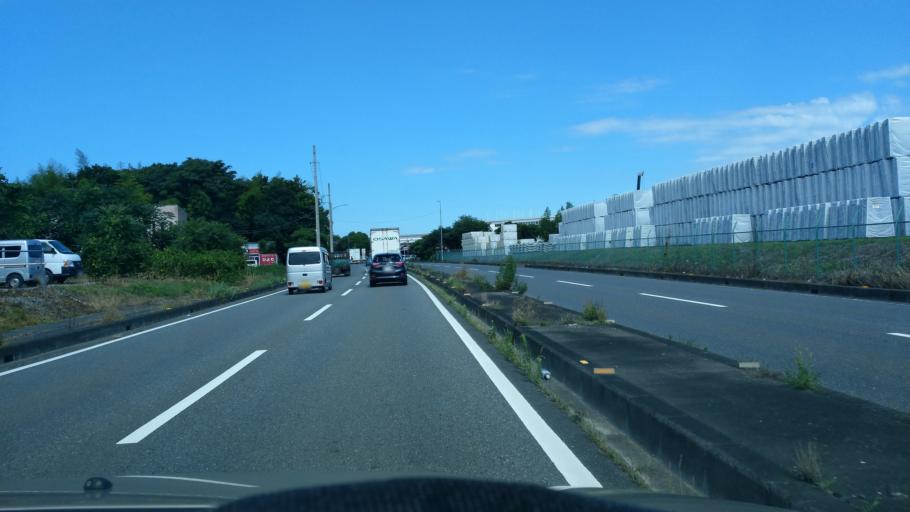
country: JP
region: Saitama
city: Ogawa
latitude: 36.0387
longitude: 139.3530
